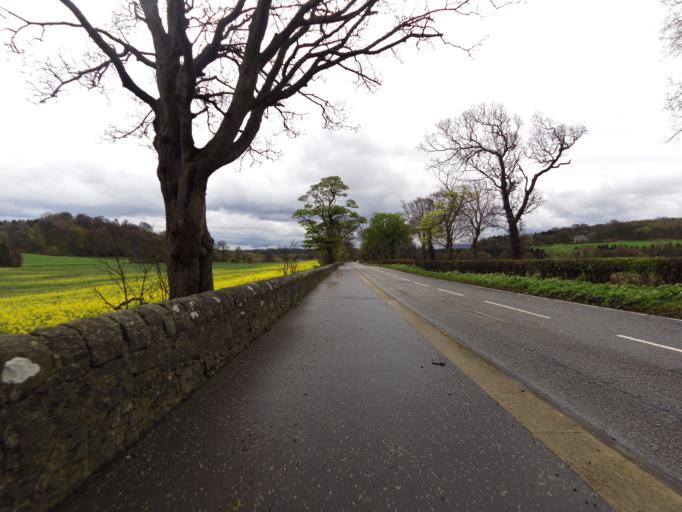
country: GB
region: Scotland
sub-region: Edinburgh
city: Queensferry
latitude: 55.9829
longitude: -3.3543
